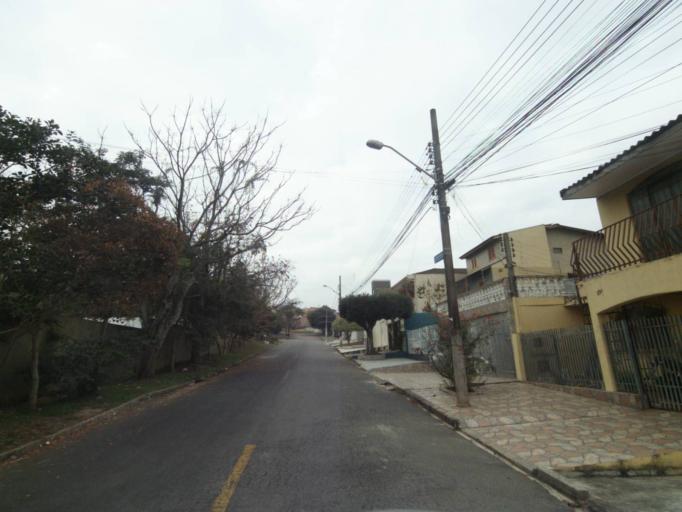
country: BR
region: Parana
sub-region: Curitiba
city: Curitiba
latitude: -25.5132
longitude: -49.3243
